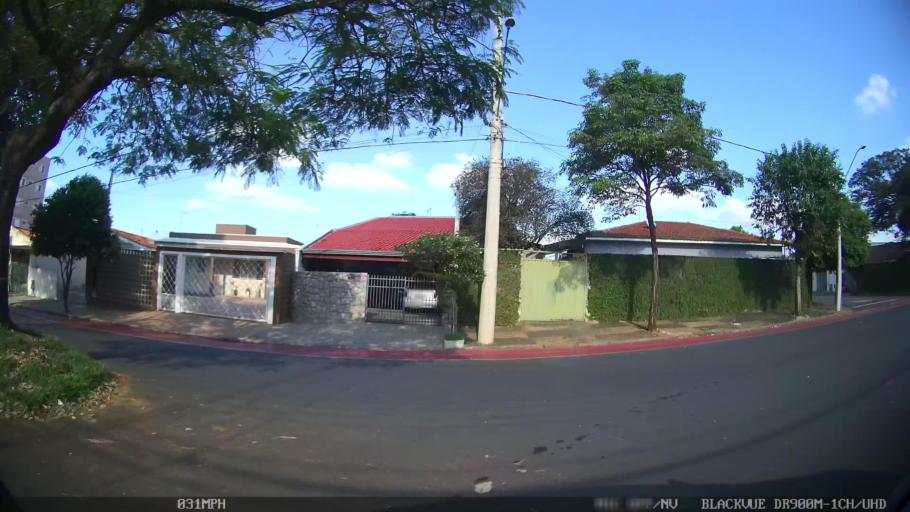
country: BR
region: Sao Paulo
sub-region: Nova Odessa
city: Nova Odessa
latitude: -22.7753
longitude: -47.3062
